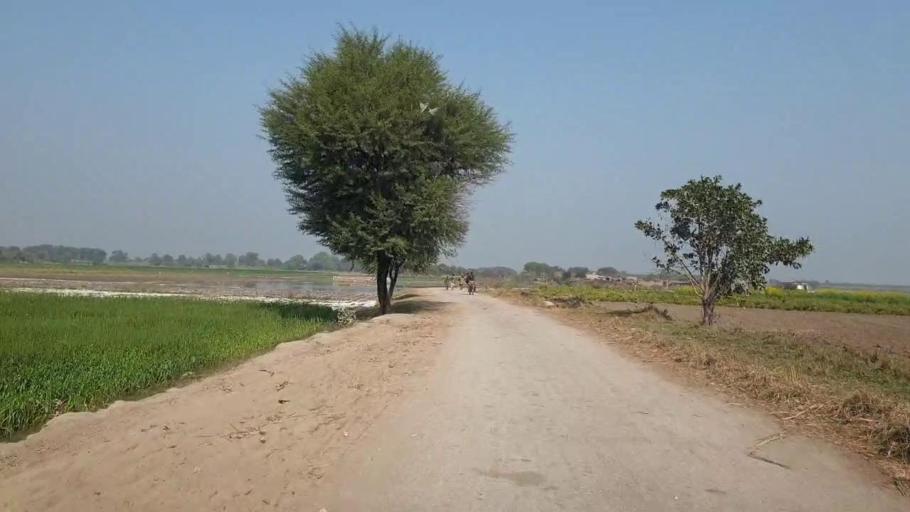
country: PK
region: Sindh
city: Bhit Shah
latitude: 25.7733
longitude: 68.5127
